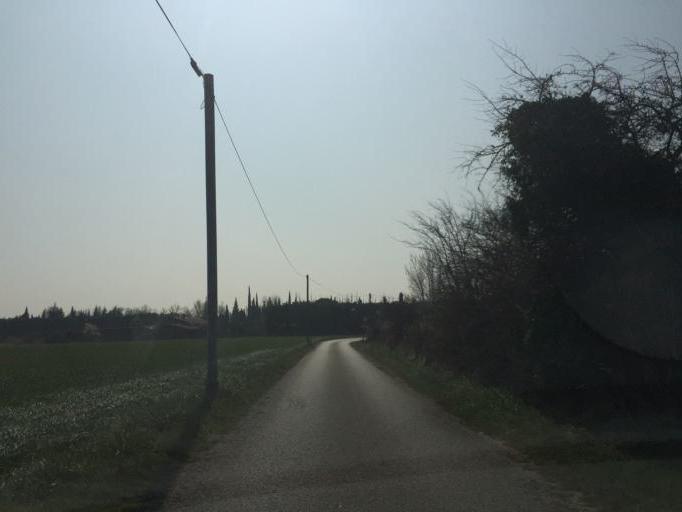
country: FR
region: Provence-Alpes-Cote d'Azur
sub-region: Departement du Vaucluse
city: Jonquieres
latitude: 44.1009
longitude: 4.9000
